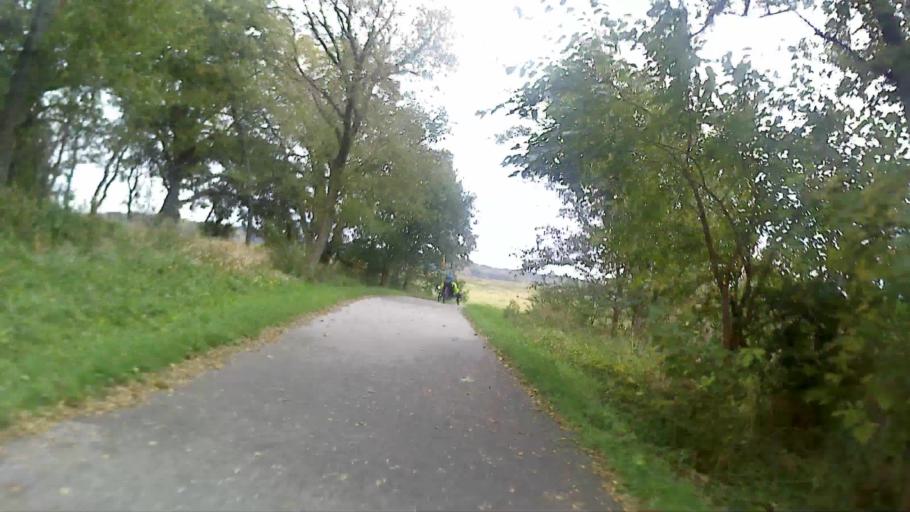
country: US
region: Illinois
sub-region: Kane County
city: Sugar Grove
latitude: 41.7942
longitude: -88.4562
